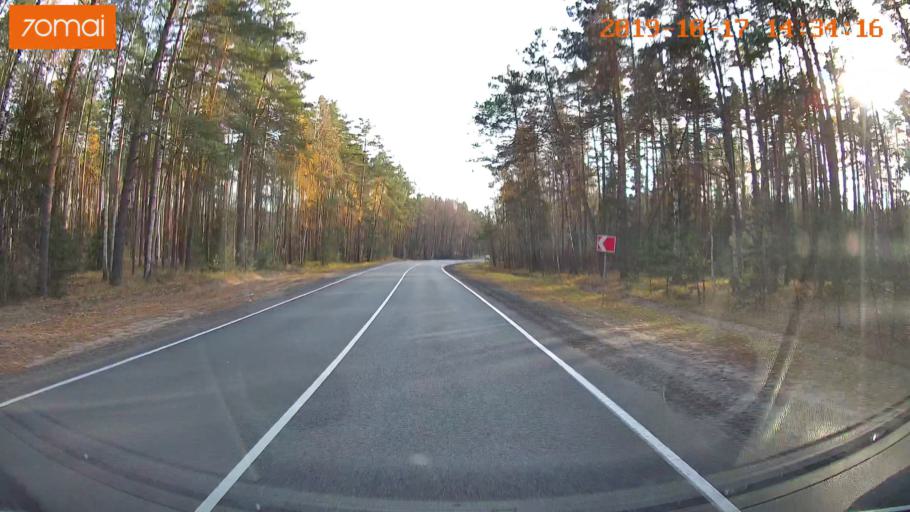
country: RU
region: Rjazan
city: Solotcha
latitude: 54.9146
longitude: 39.9975
